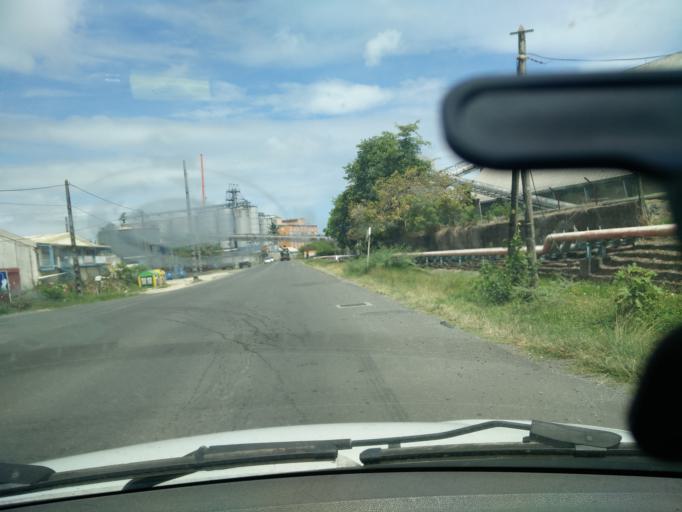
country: GP
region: Guadeloupe
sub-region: Guadeloupe
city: Pointe-a-Pitre
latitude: 16.2322
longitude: -61.5507
